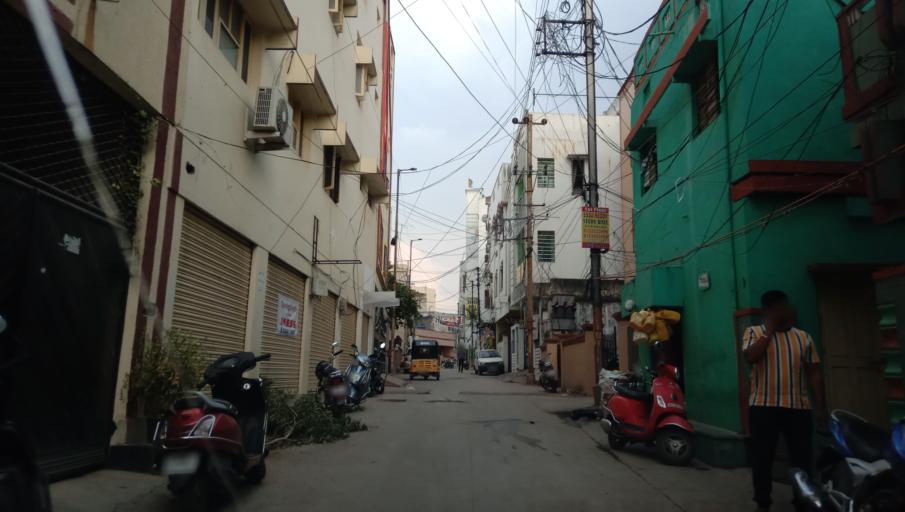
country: IN
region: Telangana
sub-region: Hyderabad
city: Hyderabad
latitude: 17.3987
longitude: 78.4861
